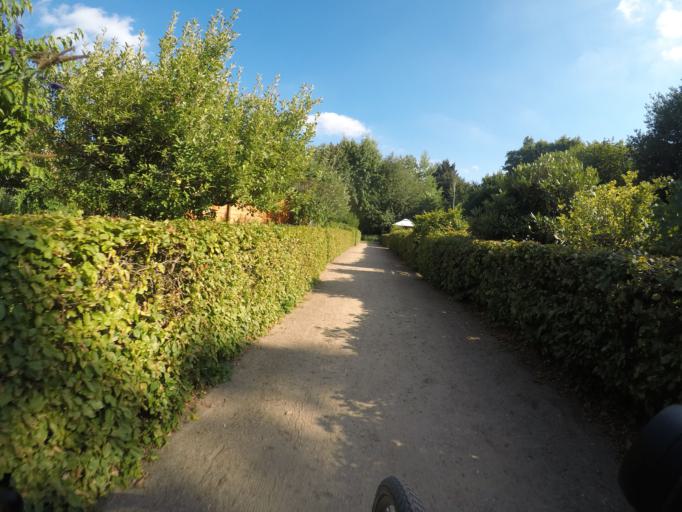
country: DE
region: Schleswig-Holstein
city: Glinde
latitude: 53.5152
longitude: 10.2037
